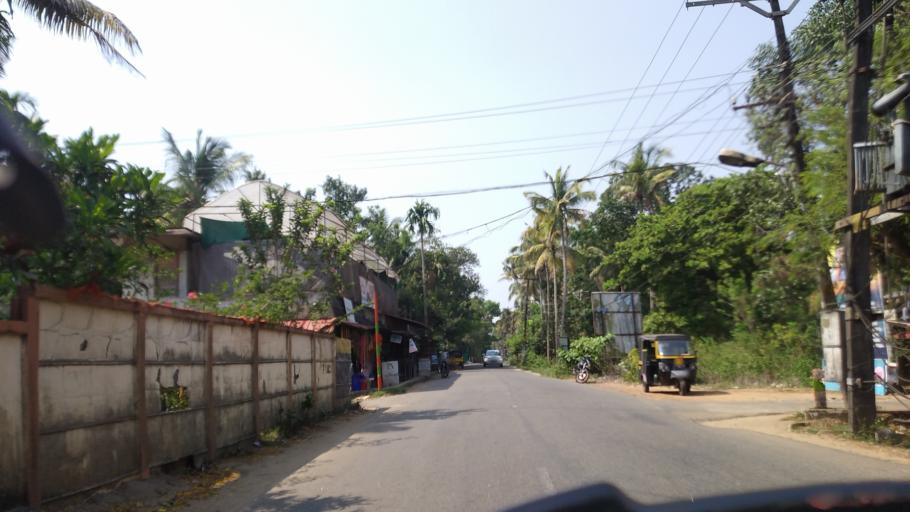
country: IN
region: Kerala
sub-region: Thrissur District
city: Kodungallur
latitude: 10.2514
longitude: 76.1481
